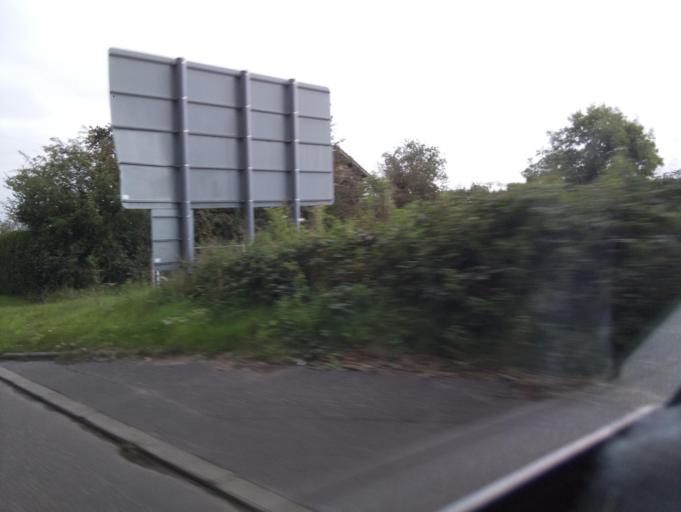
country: GB
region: Scotland
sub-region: Clackmannanshire
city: Menstrie
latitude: 56.1476
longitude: -3.9006
